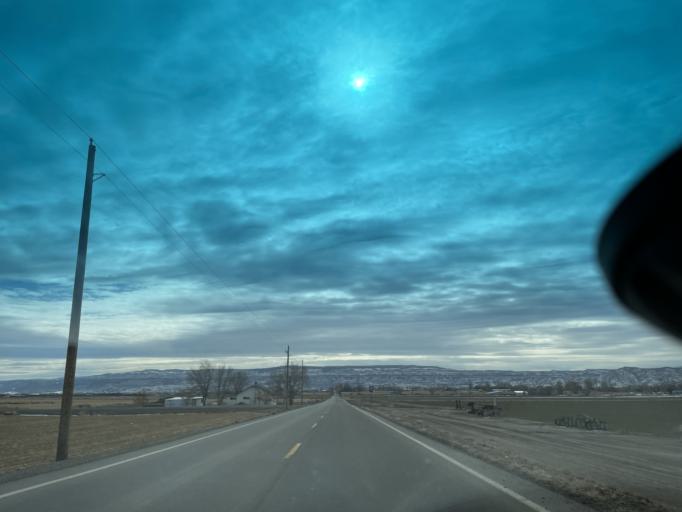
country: US
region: Colorado
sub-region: Mesa County
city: Loma
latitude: 39.2379
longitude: -108.8129
